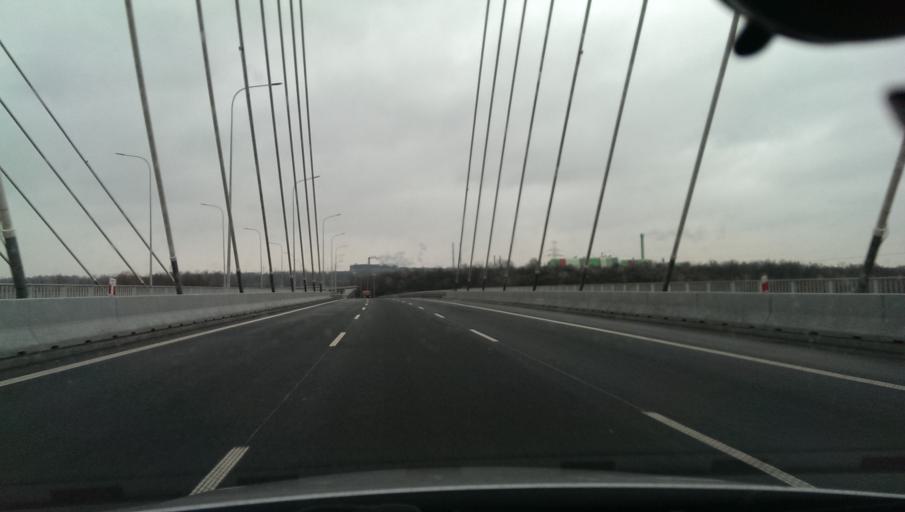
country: PL
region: Lesser Poland Voivodeship
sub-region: Powiat wielicki
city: Kokotow
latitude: 50.0521
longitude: 20.0734
